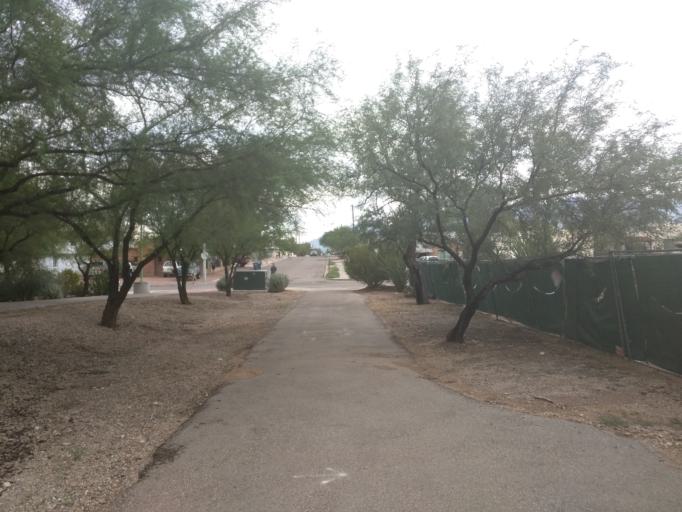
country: US
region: Arizona
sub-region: Pima County
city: Tucson
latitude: 32.2382
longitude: -110.9497
